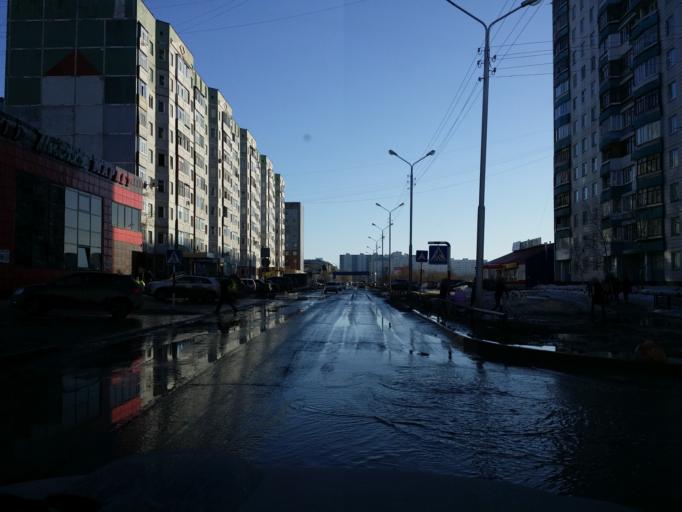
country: RU
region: Khanty-Mansiyskiy Avtonomnyy Okrug
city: Nizhnevartovsk
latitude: 60.9524
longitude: 76.5900
